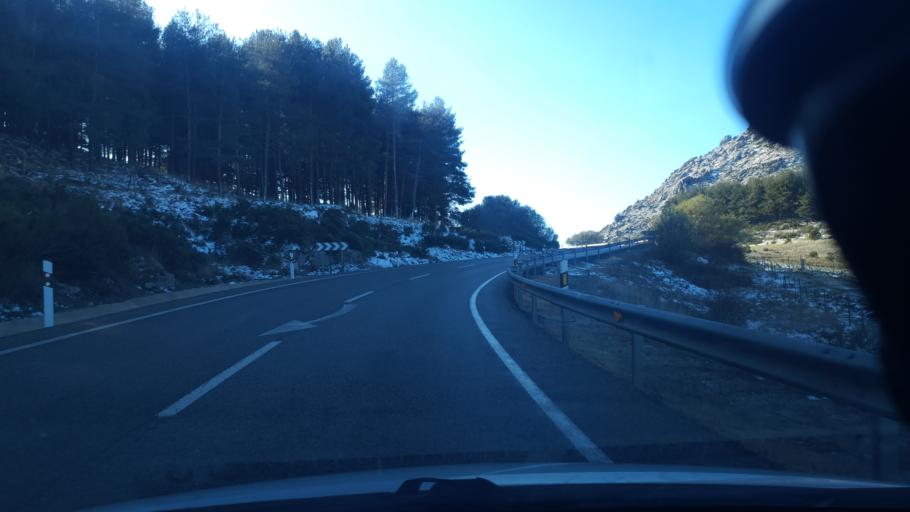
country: ES
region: Castille and Leon
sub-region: Provincia de Avila
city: Cuevas del Valle
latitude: 40.3245
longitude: -5.0134
